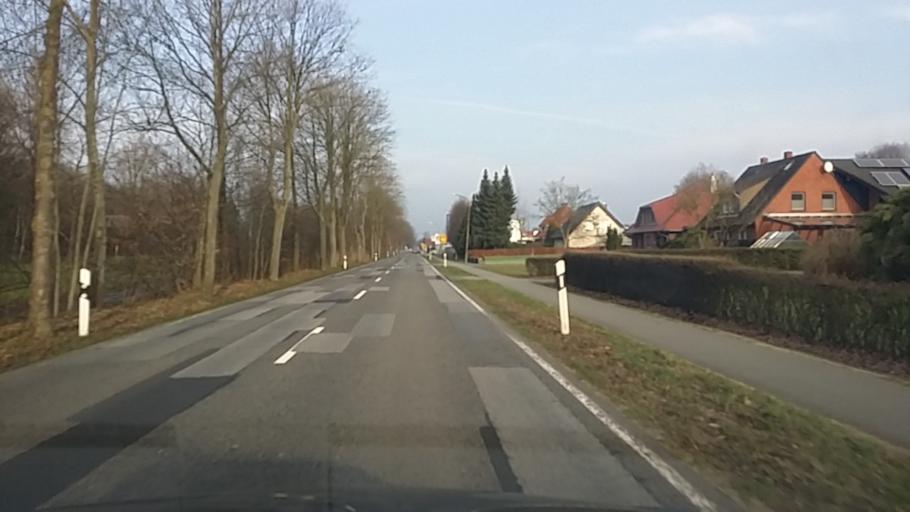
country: DE
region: Lower Saxony
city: Twist
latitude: 52.6313
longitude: 7.0983
